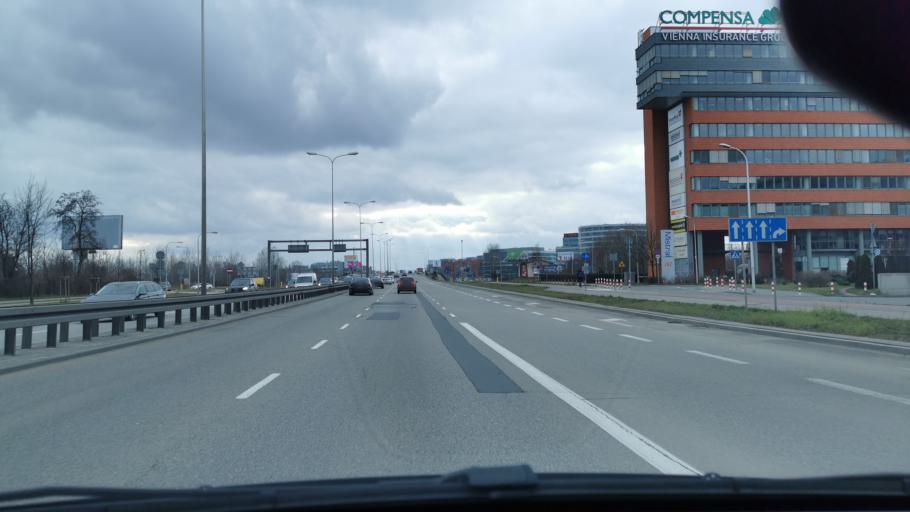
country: PL
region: Masovian Voivodeship
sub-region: Warszawa
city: Wlochy
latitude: 52.2081
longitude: 20.9460
